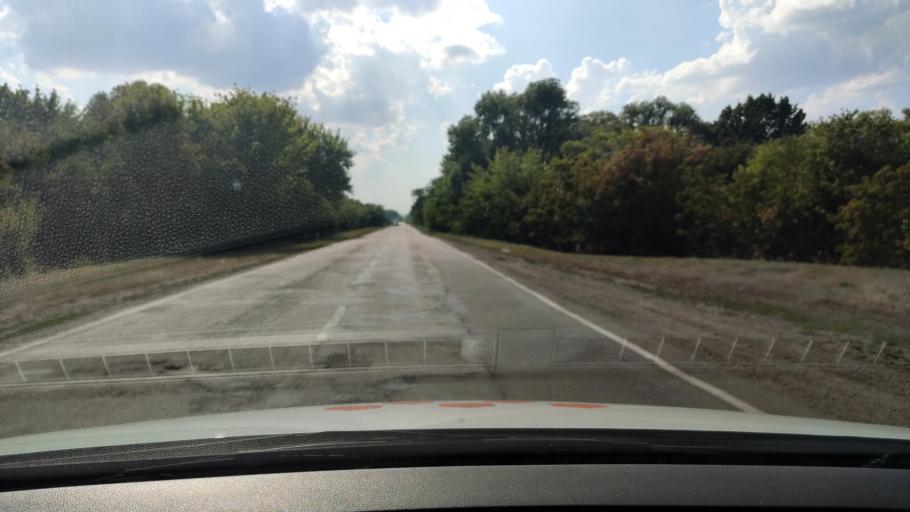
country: RU
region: Voronezj
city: Sadovoye
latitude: 51.7752
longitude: 40.5167
